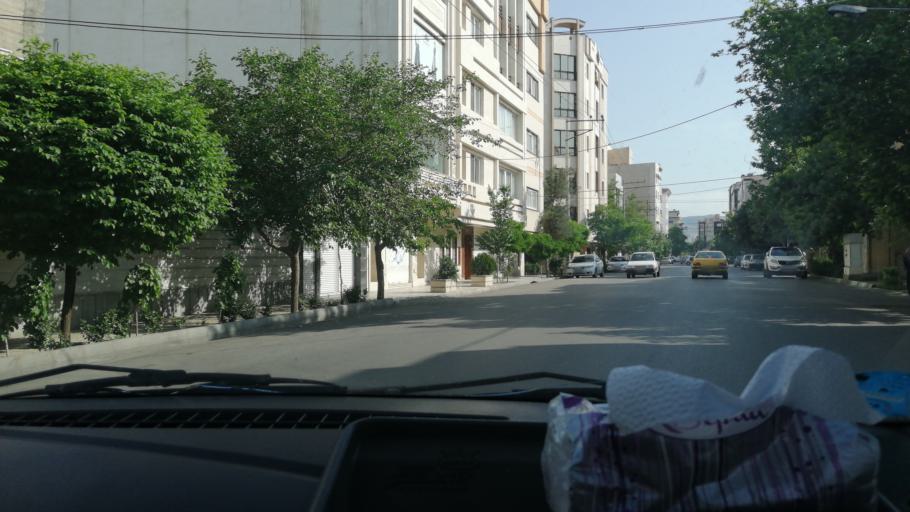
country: IR
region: Razavi Khorasan
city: Mashhad
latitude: 36.3113
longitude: 59.5614
